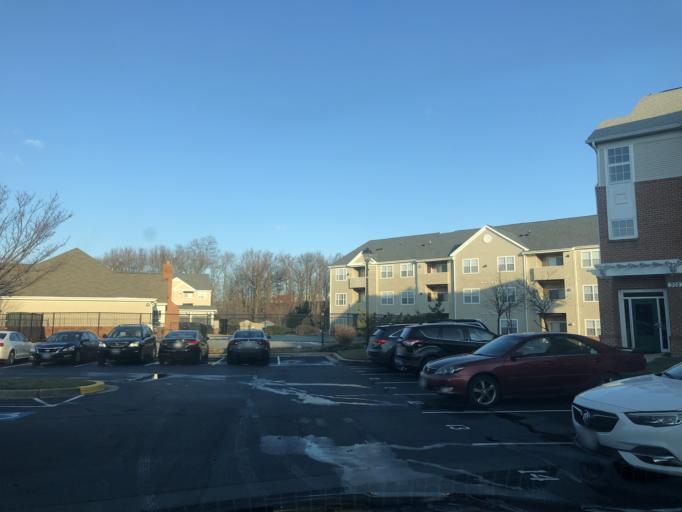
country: US
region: Maryland
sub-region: Anne Arundel County
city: Odenton
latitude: 39.0990
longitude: -76.7152
